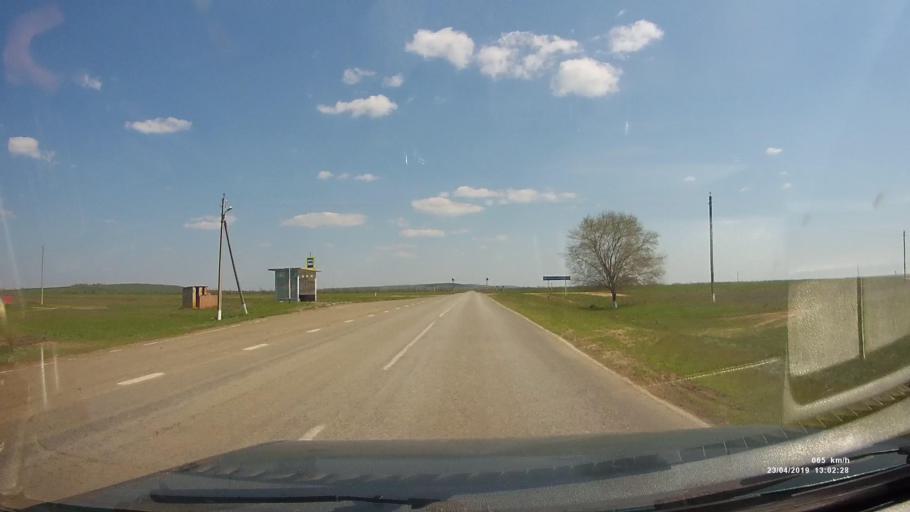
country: RU
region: Kalmykiya
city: Yashalta
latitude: 46.6004
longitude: 42.6697
